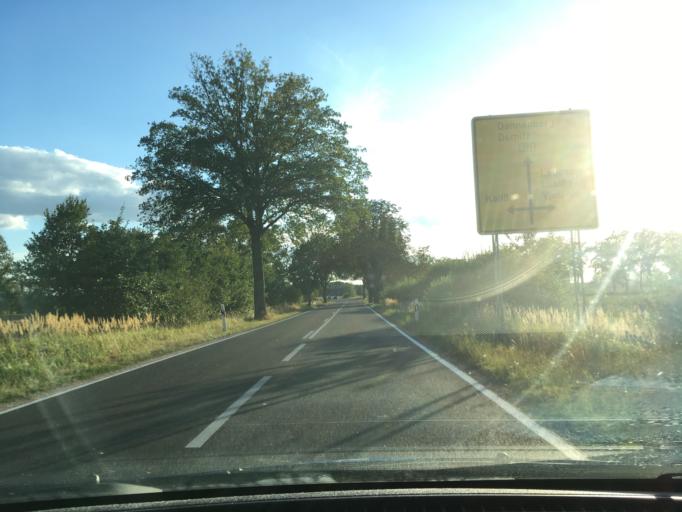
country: DE
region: Mecklenburg-Vorpommern
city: Domitz
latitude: 53.1591
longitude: 11.2460
